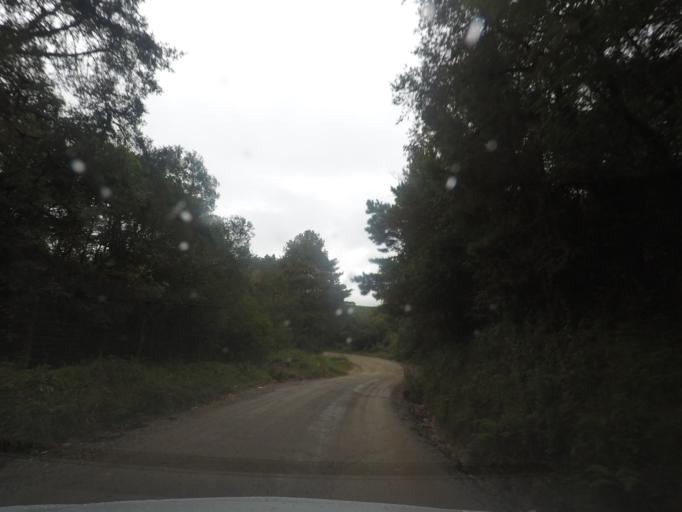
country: BR
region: Parana
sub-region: Campina Grande Do Sul
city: Campina Grande do Sul
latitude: -25.3091
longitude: -49.0963
